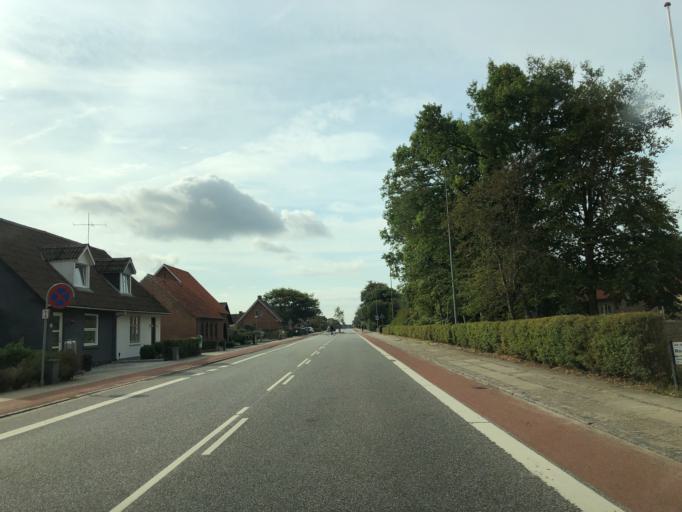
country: DK
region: Central Jutland
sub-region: Ringkobing-Skjern Kommune
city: Skjern
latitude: 55.9399
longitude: 8.5016
